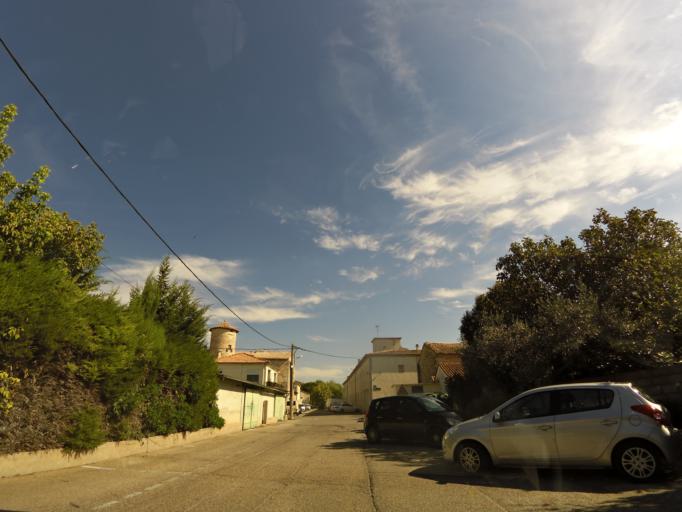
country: FR
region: Languedoc-Roussillon
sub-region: Departement du Gard
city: Vestric-et-Candiac
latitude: 43.7404
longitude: 4.2581
